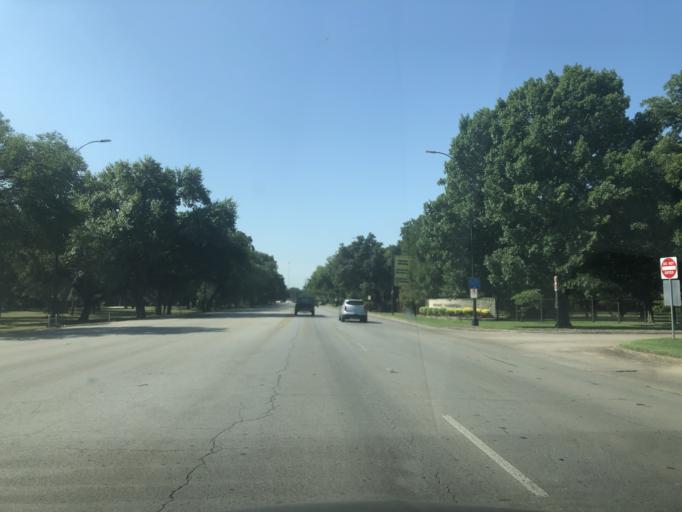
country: US
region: Texas
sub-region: Tarrant County
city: Fort Worth
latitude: 32.7405
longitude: -97.3615
